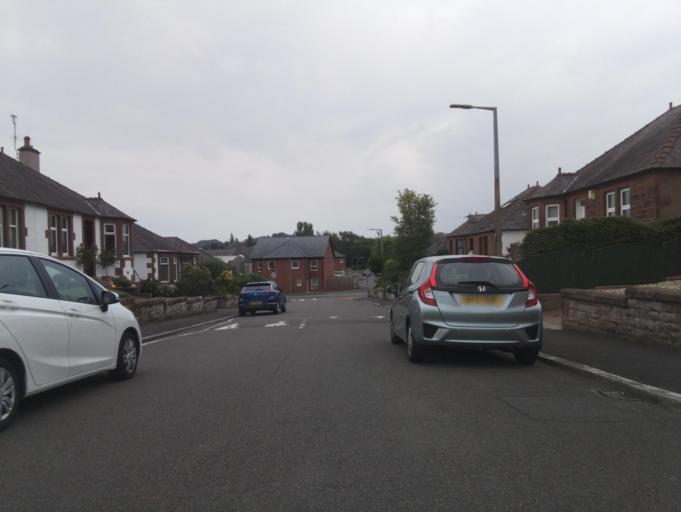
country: GB
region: Scotland
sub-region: Dumfries and Galloway
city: Dumfries
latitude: 55.0710
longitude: -3.5988
